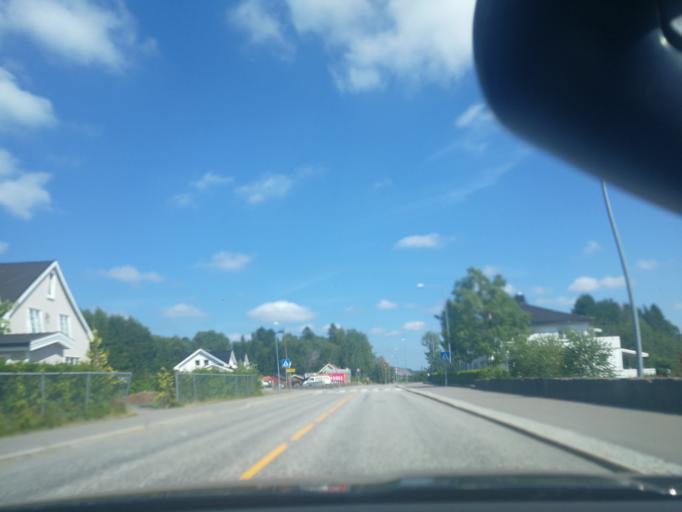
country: NO
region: Vestfold
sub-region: Stokke
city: Stokke
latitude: 59.2035
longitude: 10.2369
